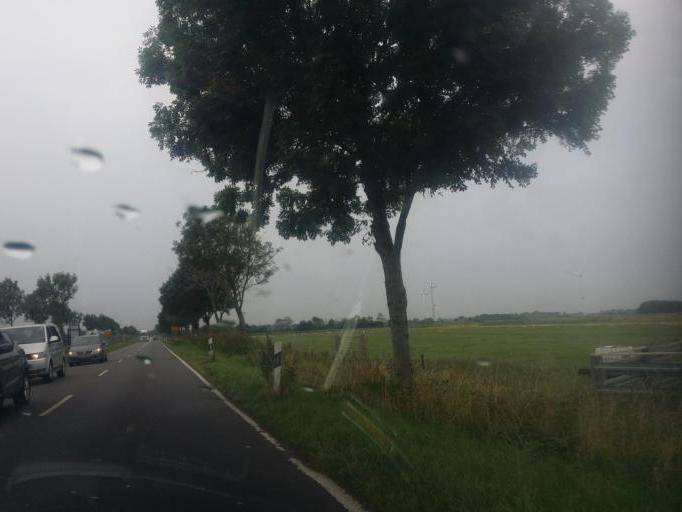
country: DE
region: Schleswig-Holstein
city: Husum
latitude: 54.4663
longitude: 9.0535
